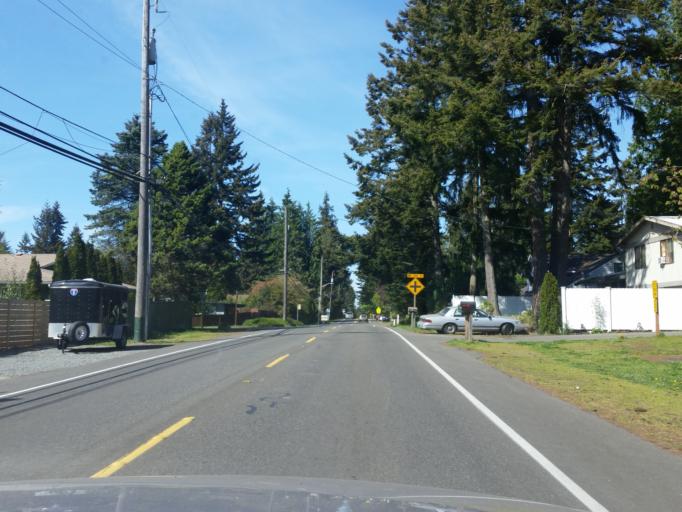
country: US
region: Washington
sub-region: Snohomish County
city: Esperance
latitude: 47.7730
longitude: -122.3612
